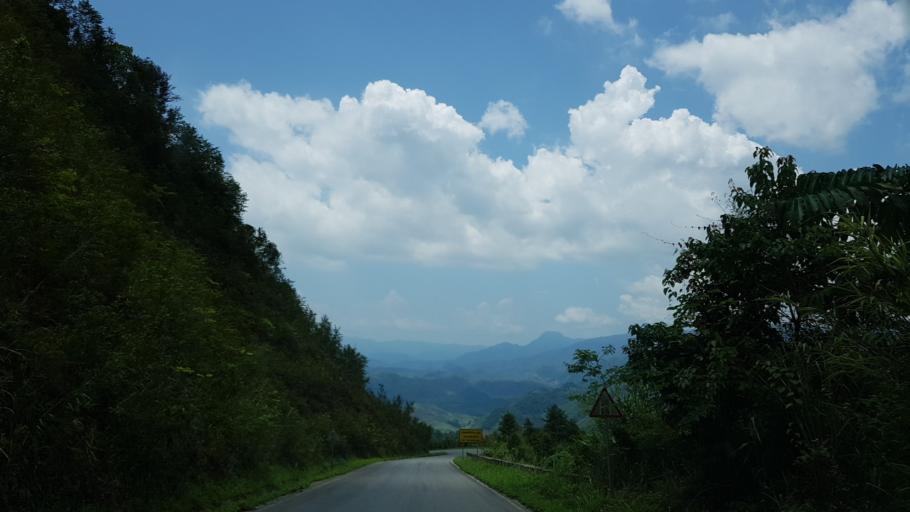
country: LA
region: Vientiane
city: Muang Kasi
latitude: 19.3739
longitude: 102.1591
